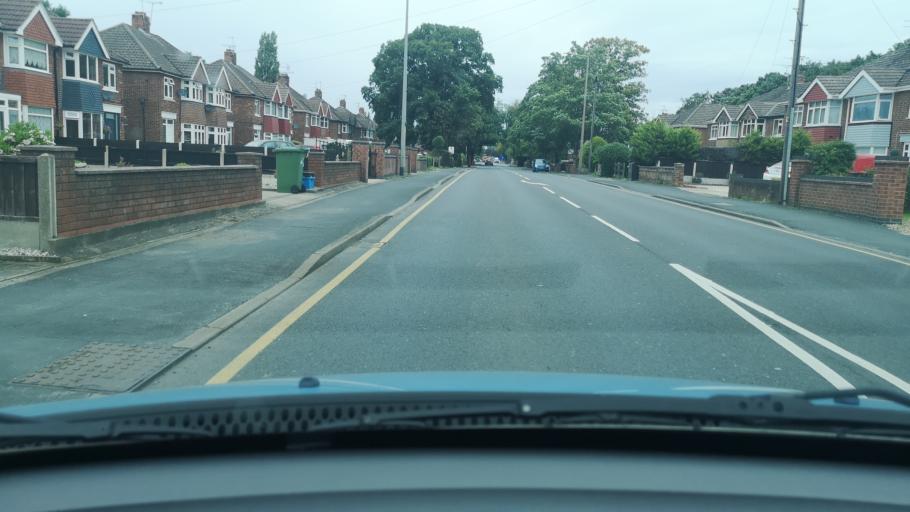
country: GB
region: England
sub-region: North Lincolnshire
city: Scunthorpe
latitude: 53.5864
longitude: -0.6842
